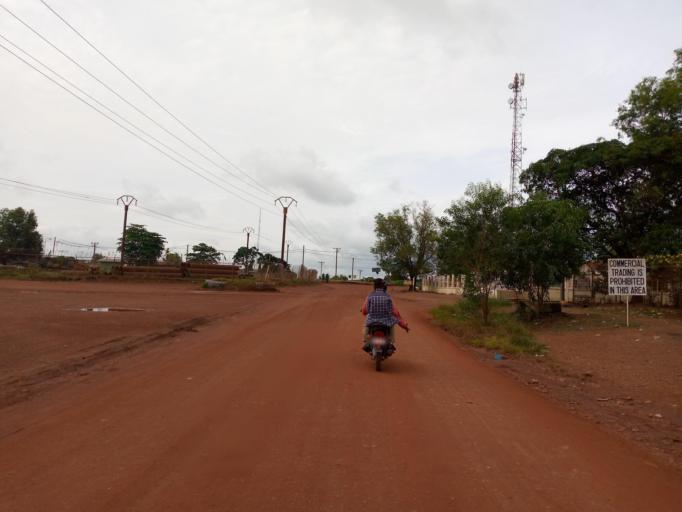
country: SL
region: Southern Province
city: Mogbwemo
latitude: 7.7669
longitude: -12.2959
